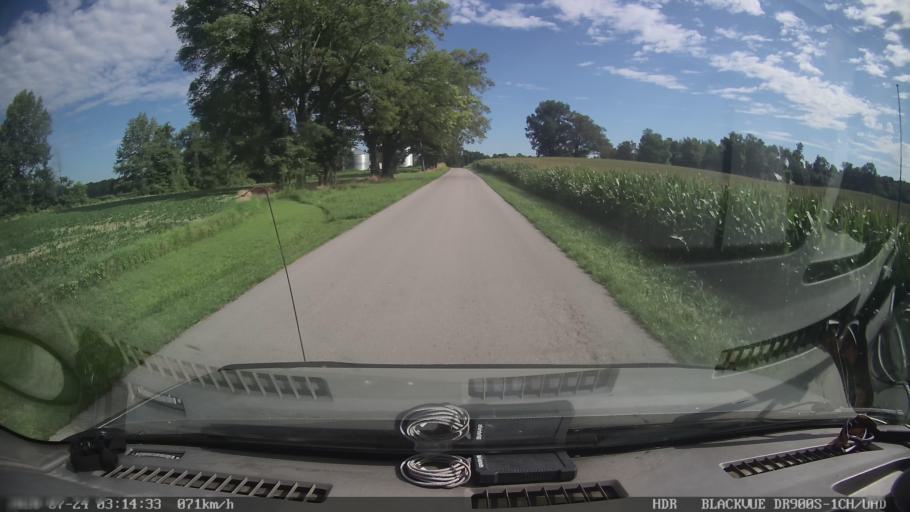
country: US
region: Kentucky
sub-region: Todd County
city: Guthrie
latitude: 36.6879
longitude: -87.1716
